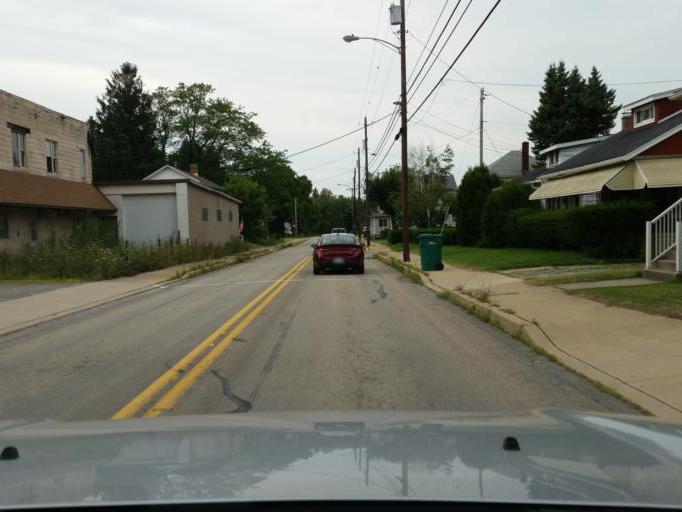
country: US
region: Pennsylvania
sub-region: Westmoreland County
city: Derry
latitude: 40.3393
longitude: -79.2993
